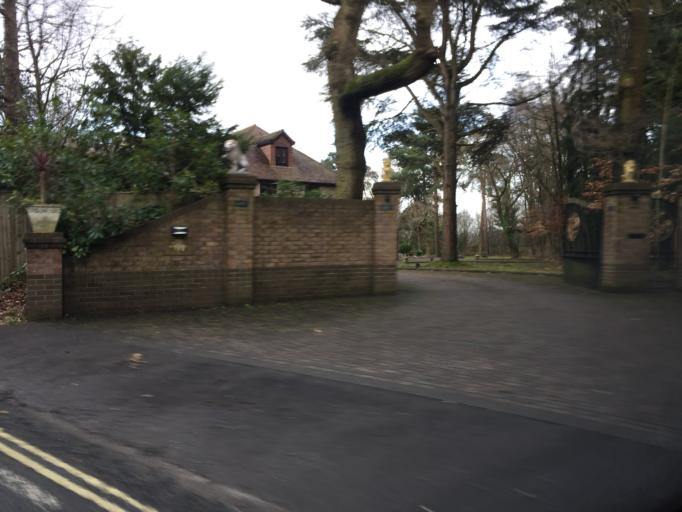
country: GB
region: England
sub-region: Hampshire
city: Eastleigh
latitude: 50.9587
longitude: -1.3991
